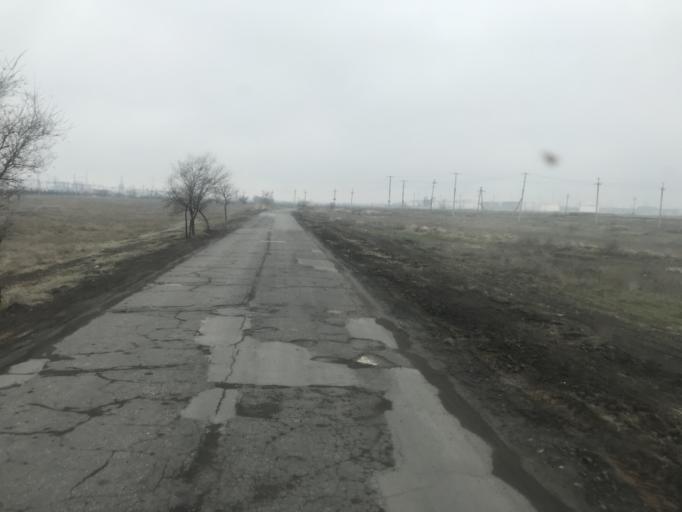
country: RU
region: Volgograd
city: Svetlyy Yar
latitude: 48.4916
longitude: 44.6588
